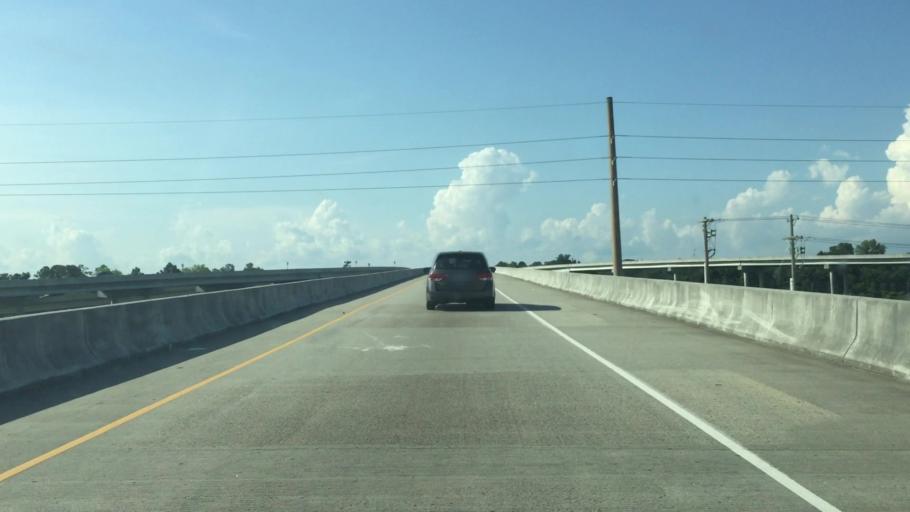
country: US
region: South Carolina
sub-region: Horry County
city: North Myrtle Beach
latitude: 33.7866
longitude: -78.7758
